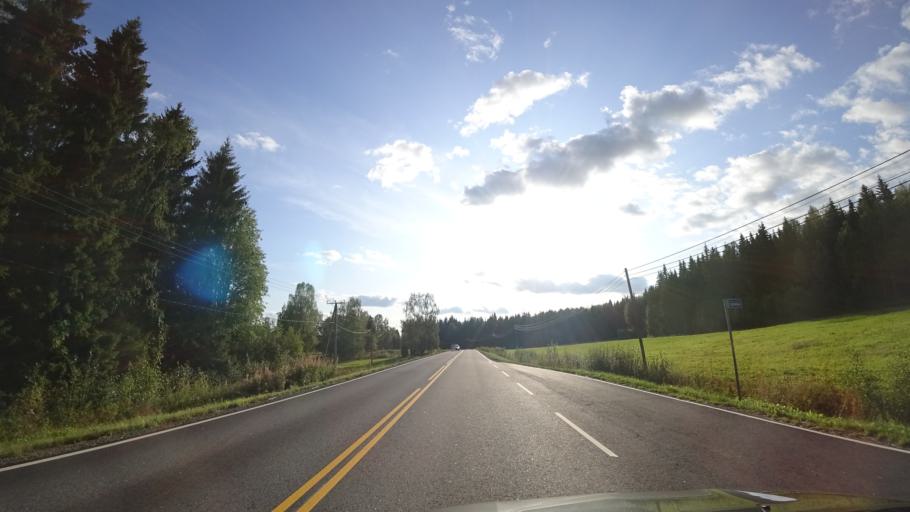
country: FI
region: Paijanne Tavastia
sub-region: Lahti
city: Haemeenkoski
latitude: 61.0855
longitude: 25.1444
